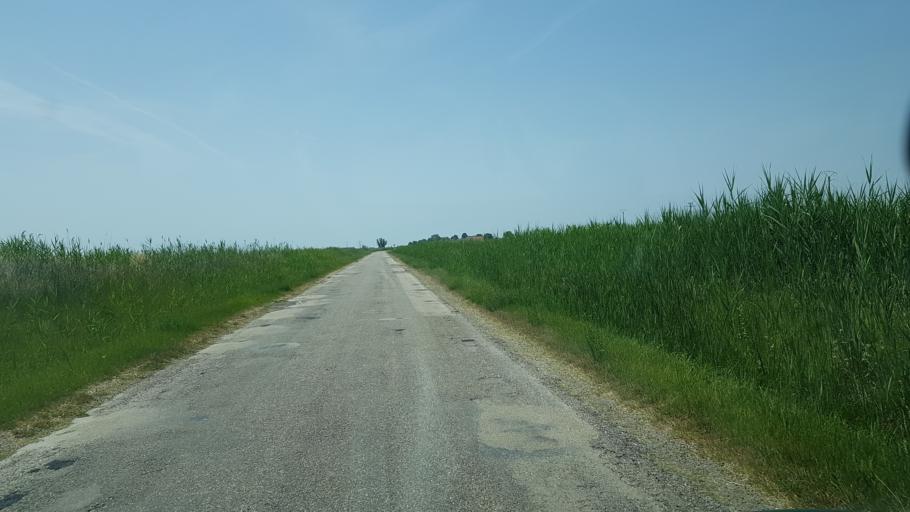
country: FR
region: Provence-Alpes-Cote d'Azur
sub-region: Departement des Bouches-du-Rhone
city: Arles
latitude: 43.6261
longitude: 4.5725
